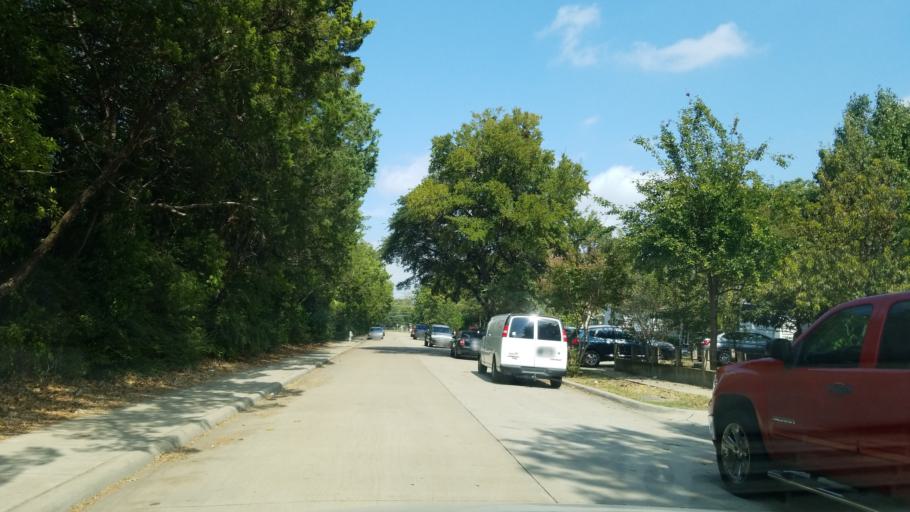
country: US
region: Texas
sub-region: Dallas County
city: Garland
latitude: 32.8923
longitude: -96.6552
